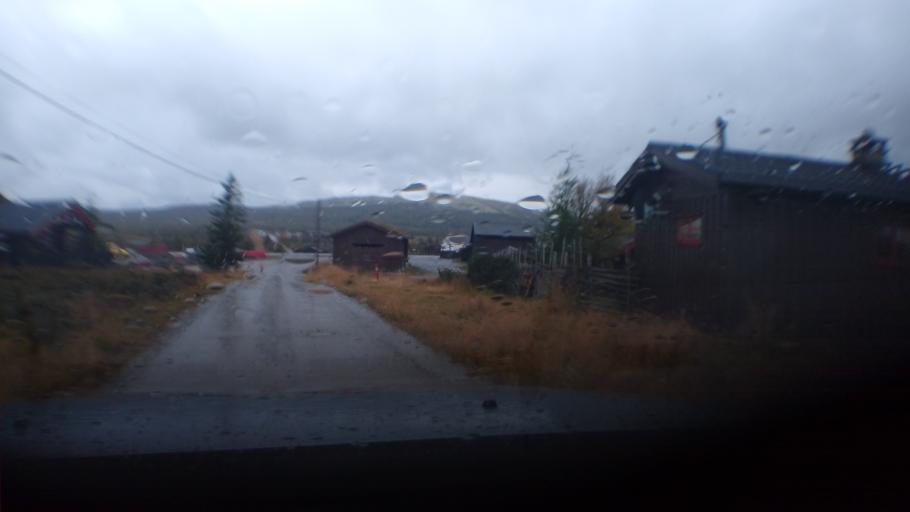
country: NO
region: Oppland
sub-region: Ringebu
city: Ringebu
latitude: 61.6491
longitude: 10.0953
